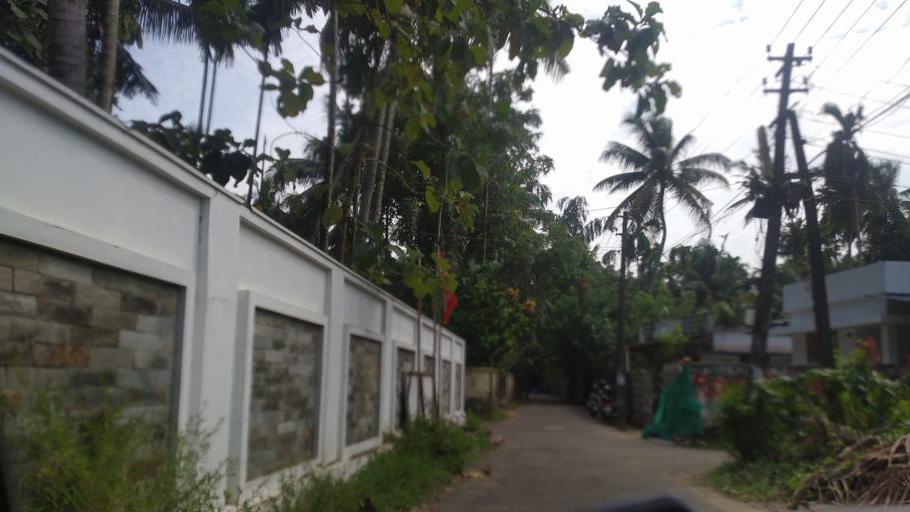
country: IN
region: Kerala
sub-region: Ernakulam
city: Elur
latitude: 10.0874
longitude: 76.2103
